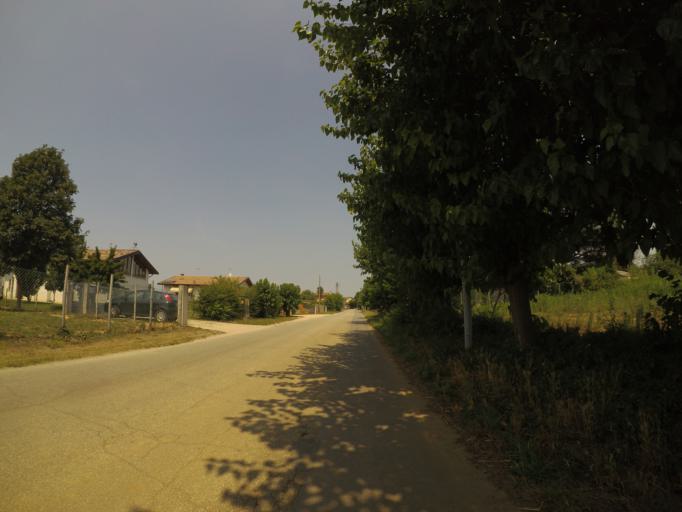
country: IT
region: Friuli Venezia Giulia
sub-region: Provincia di Udine
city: Basiliano-Vissandone
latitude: 46.0343
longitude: 13.1045
